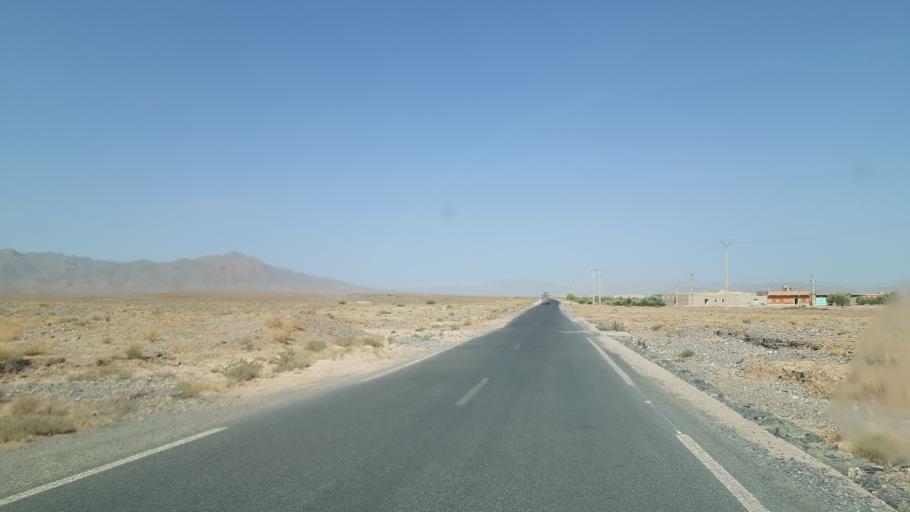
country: MA
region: Meknes-Tafilalet
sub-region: Errachidia
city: Amouguer
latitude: 32.2367
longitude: -4.6231
